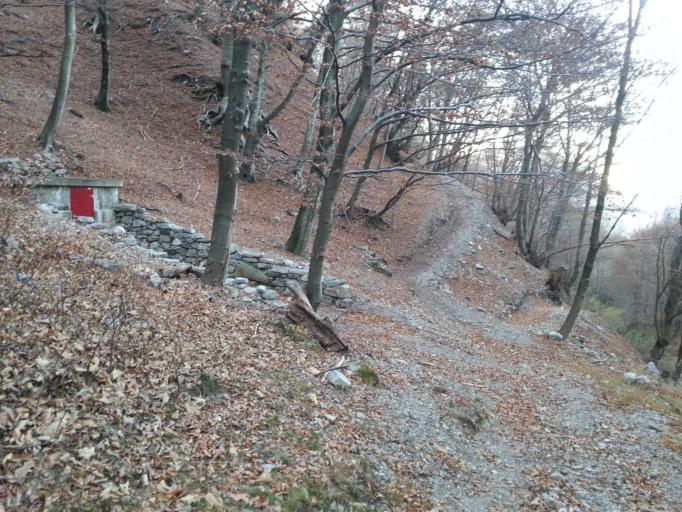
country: CH
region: Ticino
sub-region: Lugano District
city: Pregassona
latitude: 46.0194
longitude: 9.0002
